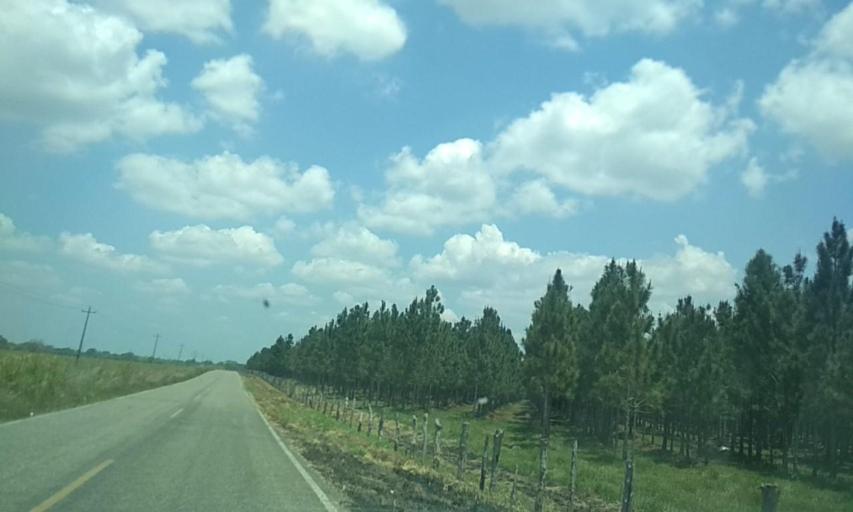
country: MX
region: Tabasco
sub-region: Huimanguillo
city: Huapacal 1ra. Seccion
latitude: 17.7562
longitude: -93.7657
